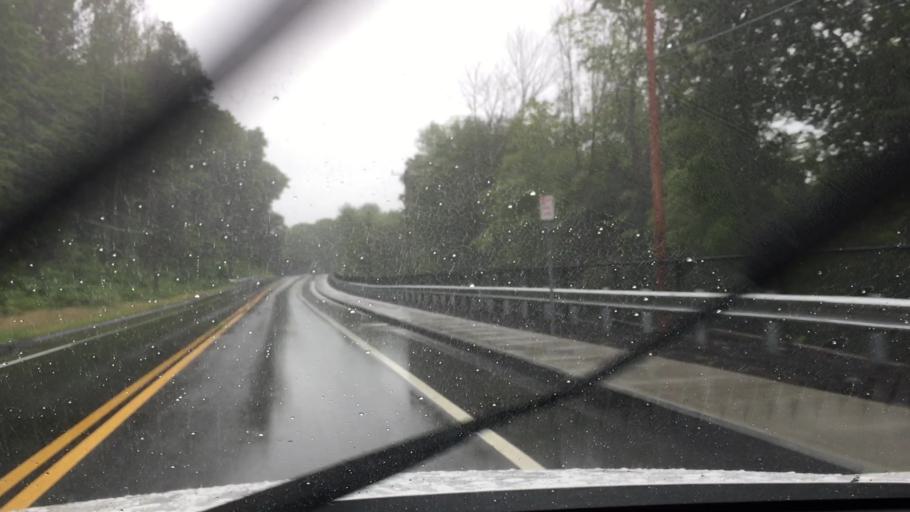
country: US
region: Massachusetts
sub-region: Berkshire County
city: Dalton
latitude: 42.4702
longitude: -73.1632
